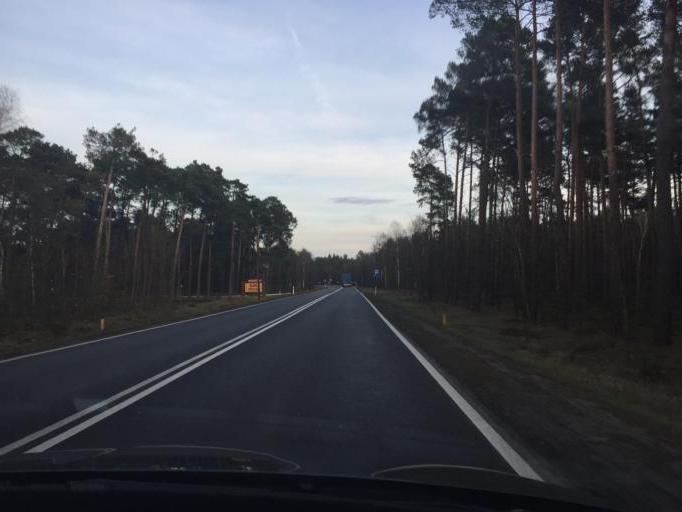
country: PL
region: Lubusz
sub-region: Powiat zielonogorski
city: Nowogrod Bobrzanski
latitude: 51.8225
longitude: 15.2983
